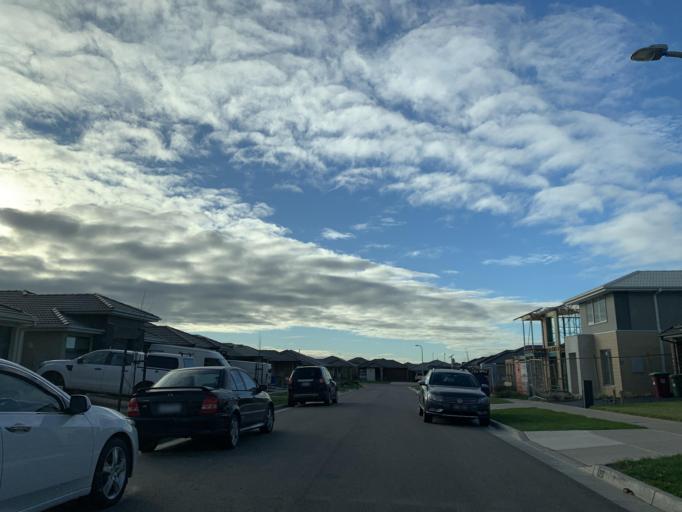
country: AU
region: Victoria
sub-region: Casey
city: Junction Village
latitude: -38.1304
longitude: 145.3135
